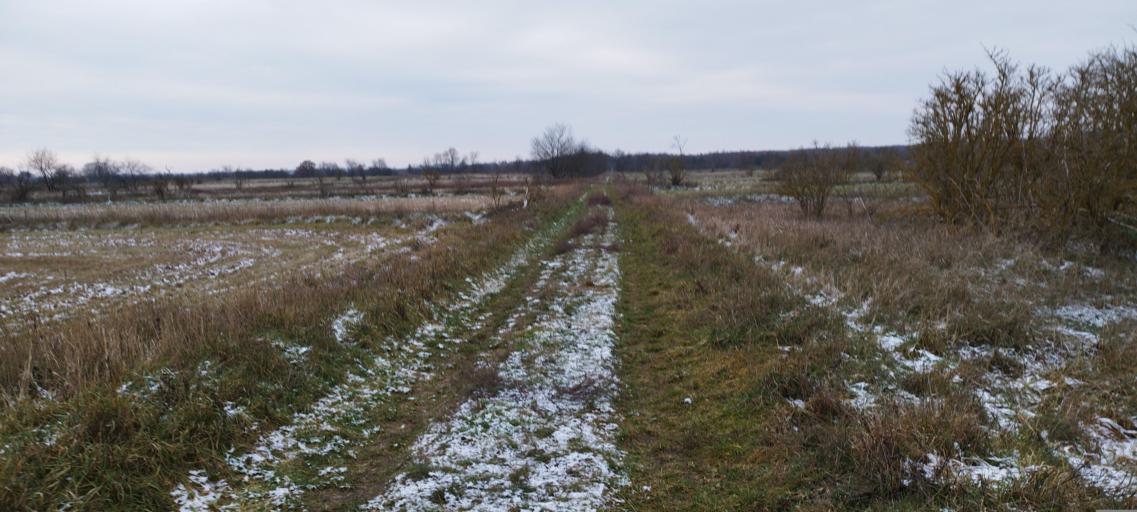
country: DE
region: Brandenburg
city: Schulzendorf
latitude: 52.3128
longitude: 13.5716
